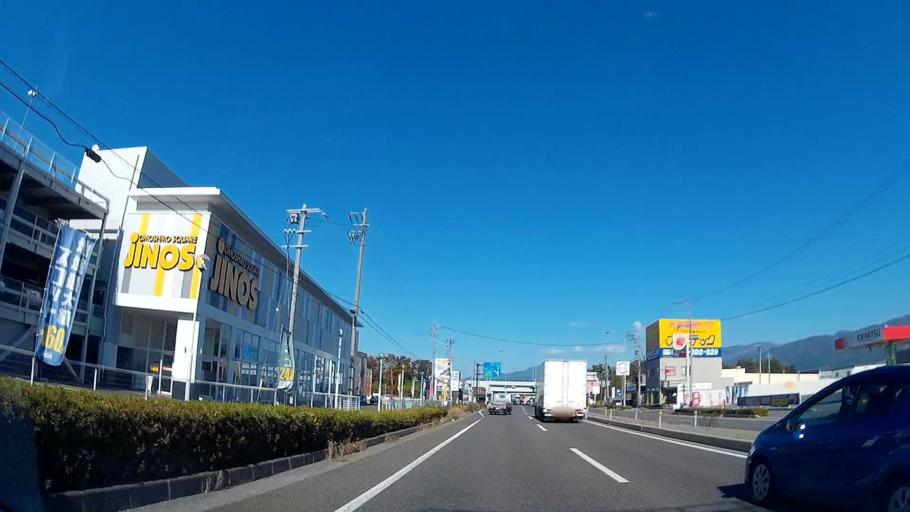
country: JP
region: Nagano
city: Shiojiri
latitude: 36.1663
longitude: 137.9539
